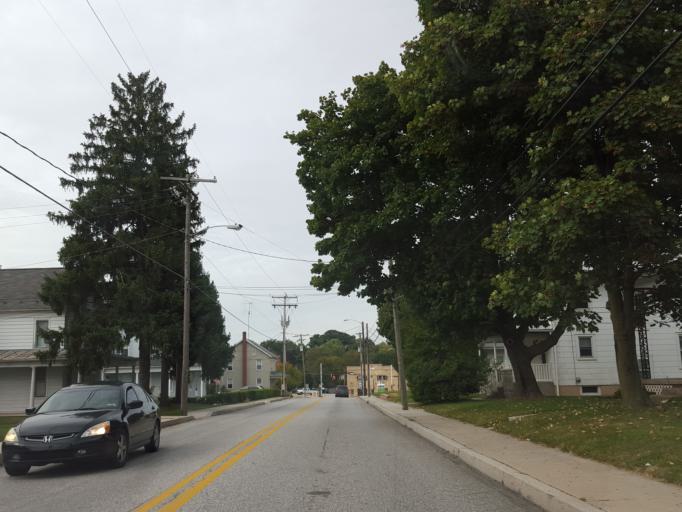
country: US
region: Pennsylvania
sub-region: York County
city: West York
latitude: 39.9022
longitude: -76.7874
